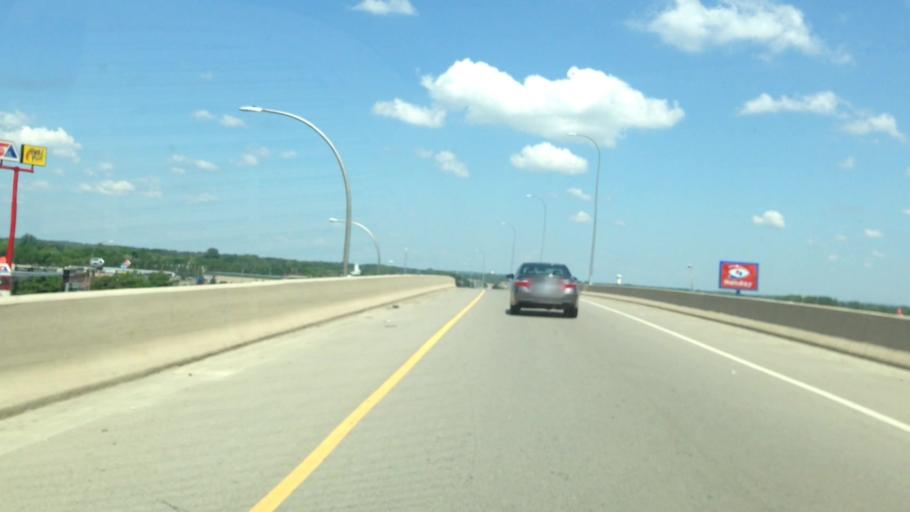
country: US
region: Minnesota
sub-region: Hennepin County
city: Rogers
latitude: 45.1985
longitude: -93.5519
